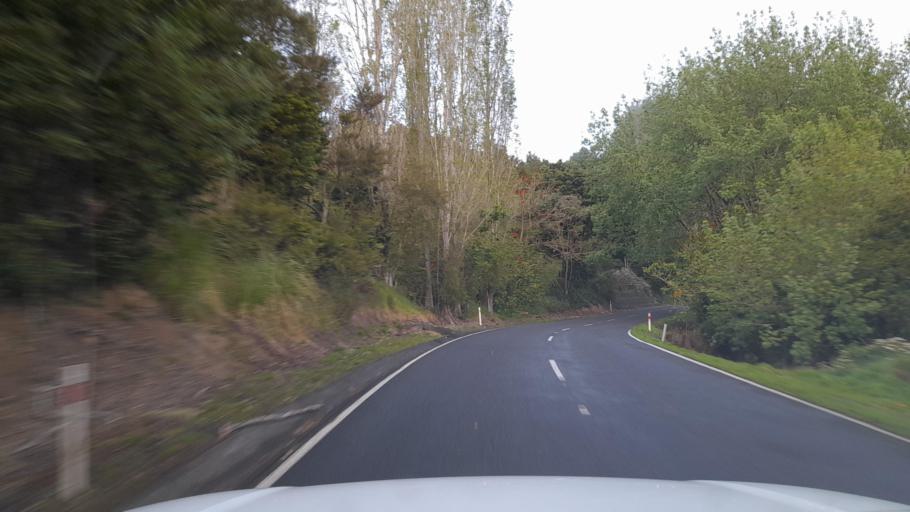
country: NZ
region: Northland
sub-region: Kaipara District
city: Dargaville
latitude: -35.7082
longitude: 173.9285
